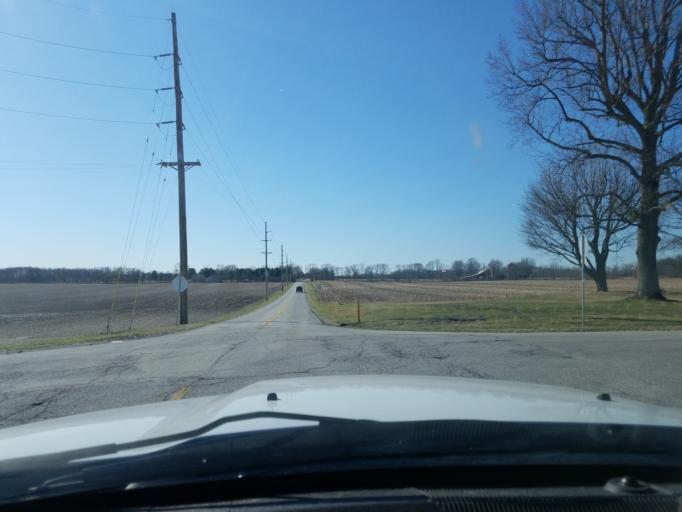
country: US
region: Indiana
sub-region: Johnson County
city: Franklin
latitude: 39.4964
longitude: -86.0077
